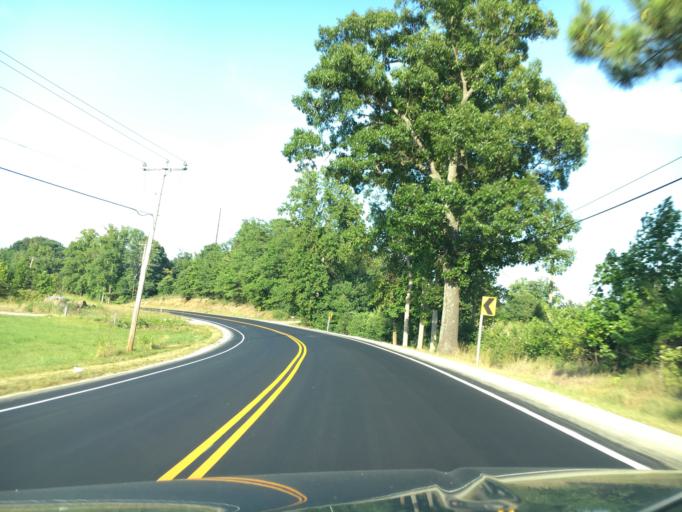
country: US
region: Virginia
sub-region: Franklin County
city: Union Hall
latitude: 36.9855
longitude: -79.7305
